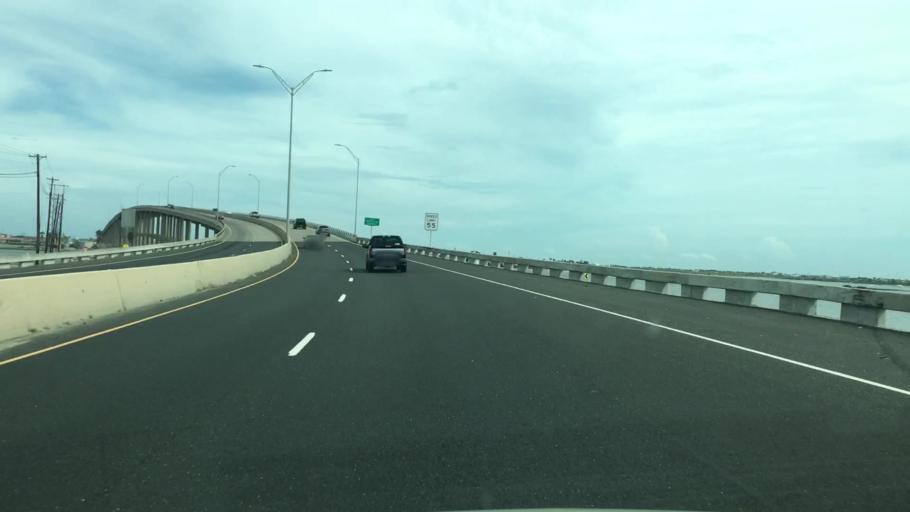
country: US
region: Texas
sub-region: Nueces County
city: Corpus Christi
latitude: 27.6375
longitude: -97.2452
